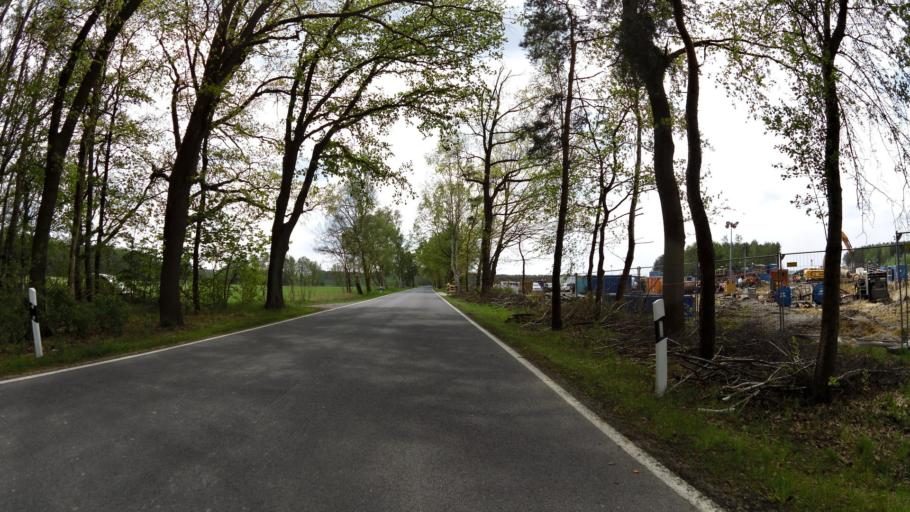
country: DE
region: Brandenburg
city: Bestensee
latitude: 52.2712
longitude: 13.7337
